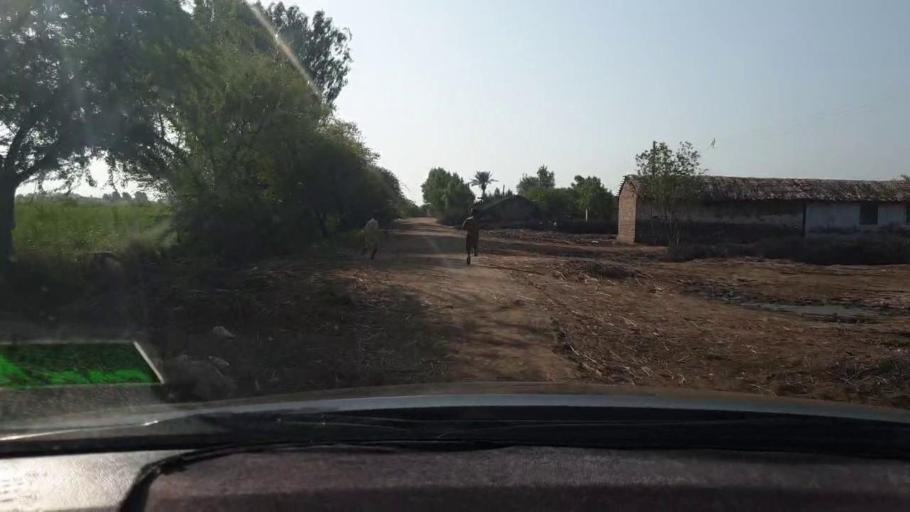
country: PK
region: Sindh
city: Tando Bago
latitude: 24.8006
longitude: 69.0183
